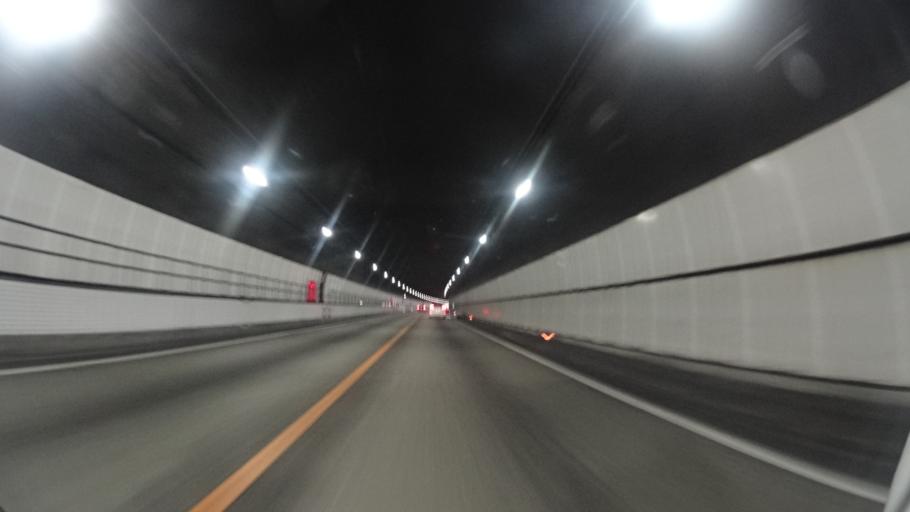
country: JP
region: Osaka
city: Takatsuki
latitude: 34.8722
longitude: 135.6533
